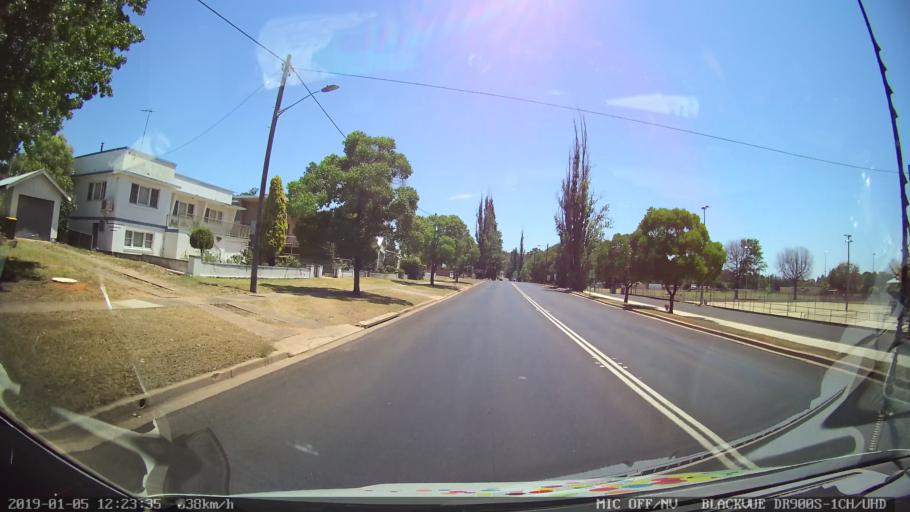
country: AU
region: New South Wales
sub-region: Warrumbungle Shire
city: Coonabarabran
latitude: -31.2705
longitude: 149.2762
